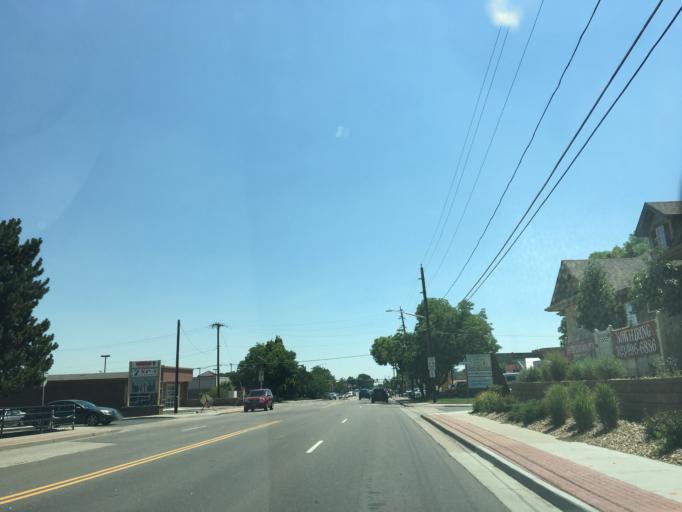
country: US
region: Colorado
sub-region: Jefferson County
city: Wheat Ridge
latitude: 39.7766
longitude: -105.0844
